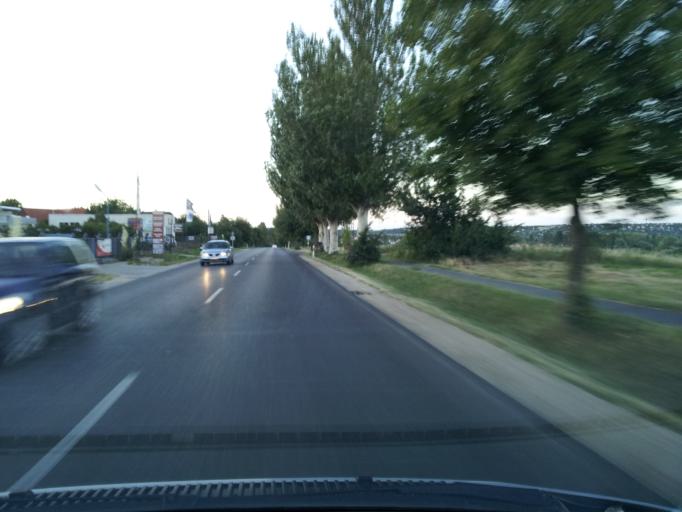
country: HU
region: Veszprem
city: Balatonalmadi
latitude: 47.0506
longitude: 18.0173
